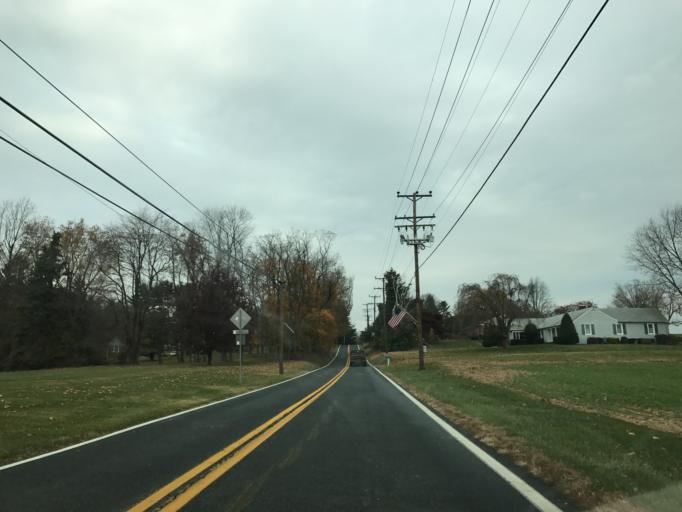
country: US
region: Maryland
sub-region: Baltimore County
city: Carney
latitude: 39.4813
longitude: -76.5189
